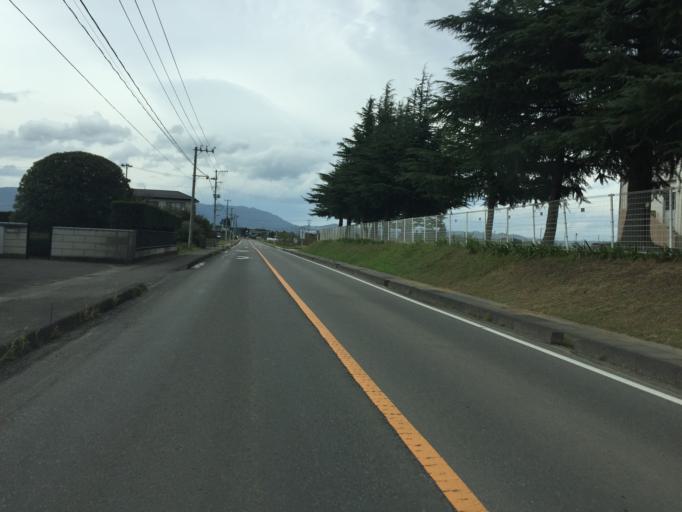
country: JP
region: Fukushima
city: Hobaramachi
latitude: 37.8329
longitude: 140.5580
